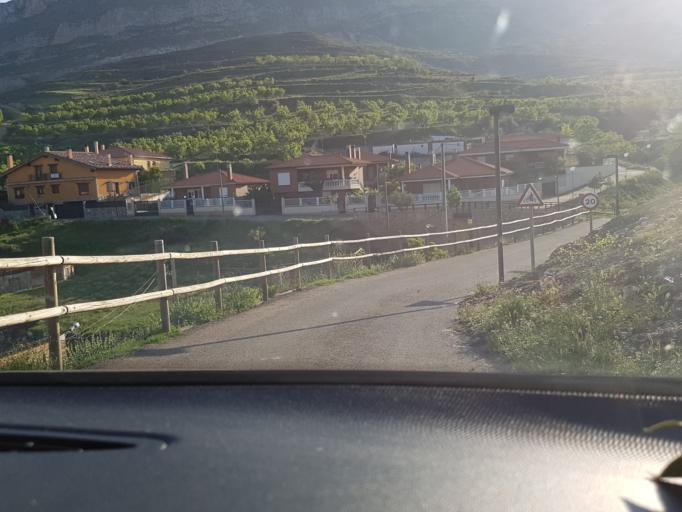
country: ES
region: La Rioja
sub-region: Provincia de La Rioja
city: Prejano
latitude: 42.1875
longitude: -2.1806
